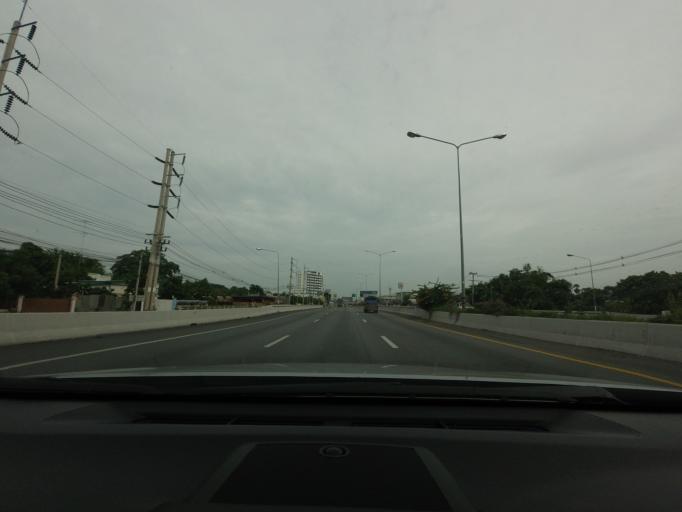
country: TH
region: Phetchaburi
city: Phetchaburi
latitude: 13.0860
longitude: 99.9435
